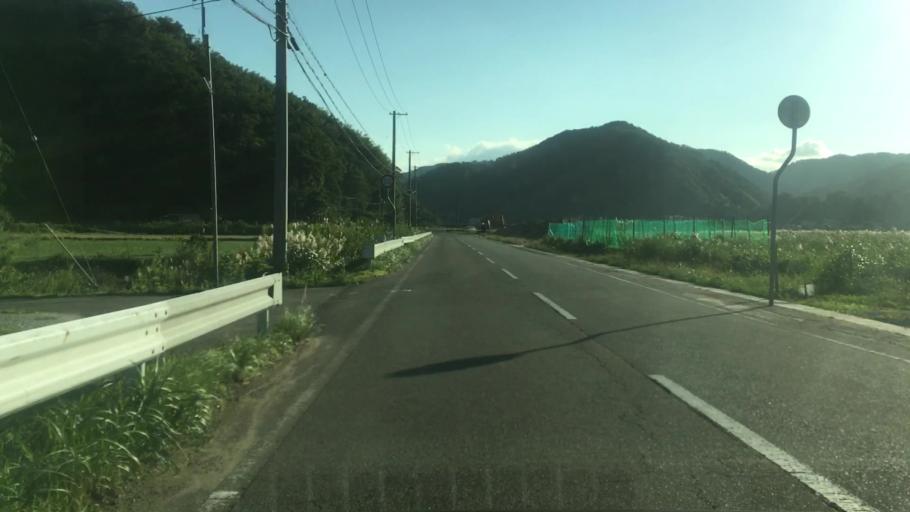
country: JP
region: Hyogo
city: Toyooka
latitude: 35.6117
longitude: 134.8098
